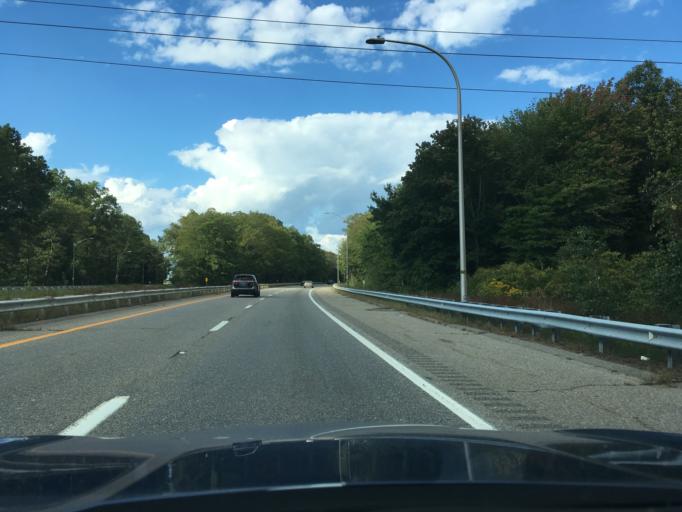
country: US
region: Massachusetts
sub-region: Bristol County
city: Seekonk
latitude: 41.8028
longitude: -71.3513
